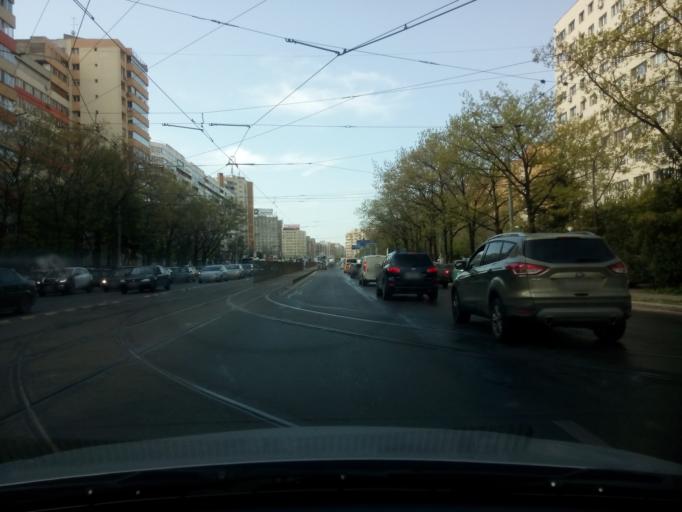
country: RO
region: Bucuresti
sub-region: Municipiul Bucuresti
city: Bucharest
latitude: 44.4528
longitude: 26.1270
